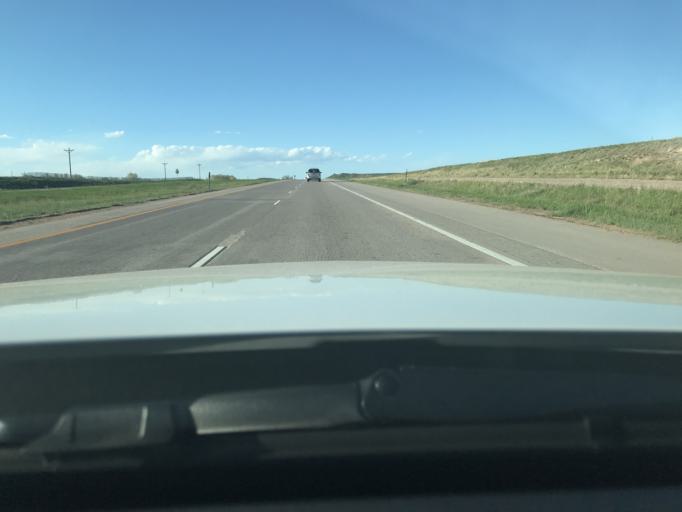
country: US
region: Wyoming
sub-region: Laramie County
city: South Greeley
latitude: 40.9465
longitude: -104.9253
